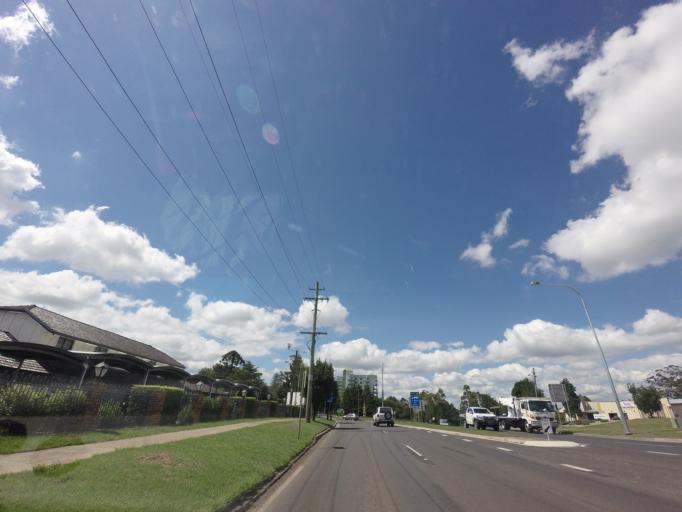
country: AU
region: Queensland
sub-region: Toowoomba
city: East Toowoomba
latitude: -27.5667
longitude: 151.9754
